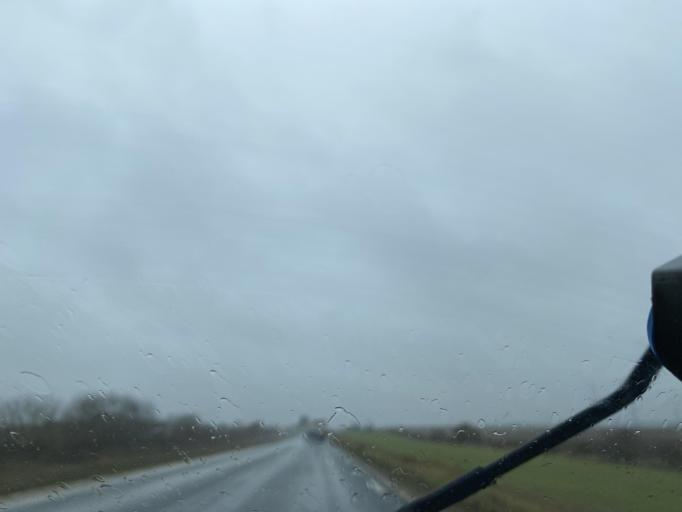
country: FR
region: Centre
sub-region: Departement d'Eure-et-Loir
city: Voves
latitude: 48.2985
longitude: 1.7020
